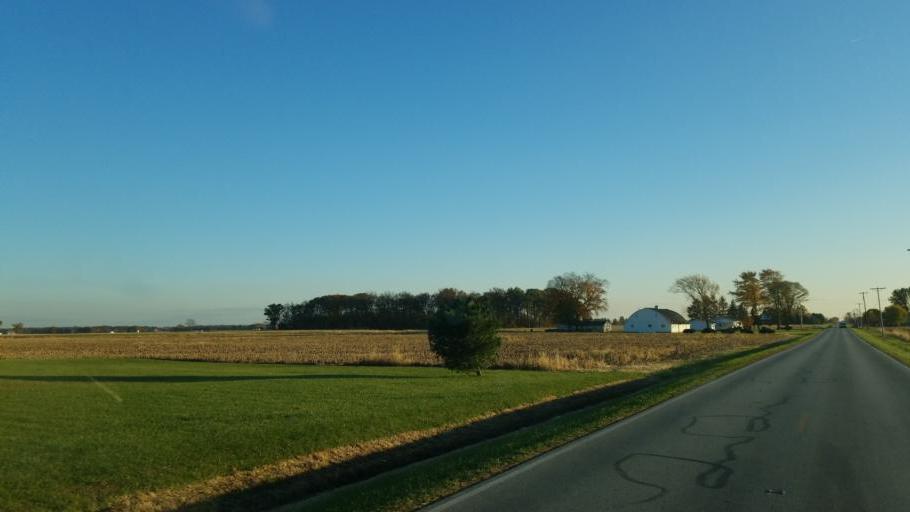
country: US
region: Ohio
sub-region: Sandusky County
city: Mount Carmel
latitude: 41.2530
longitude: -82.9753
